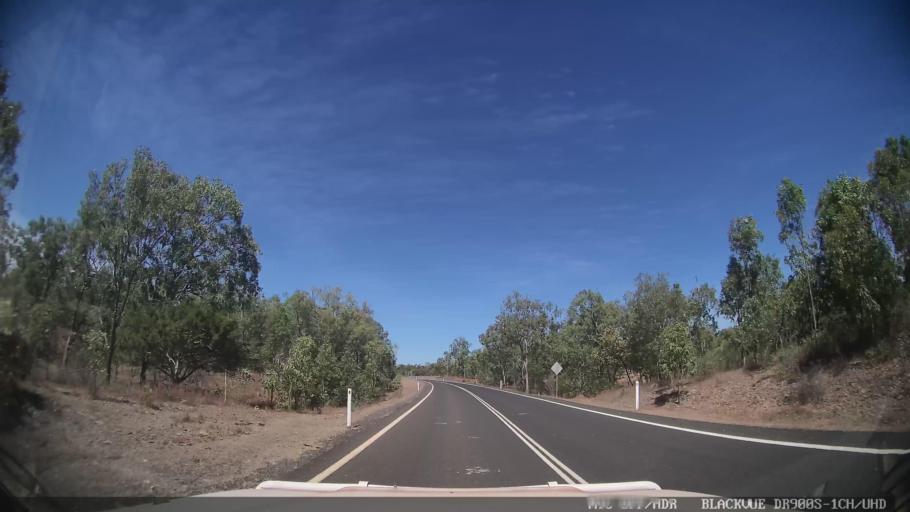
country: AU
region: Queensland
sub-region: Cook
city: Cooktown
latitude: -15.7117
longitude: 144.6154
